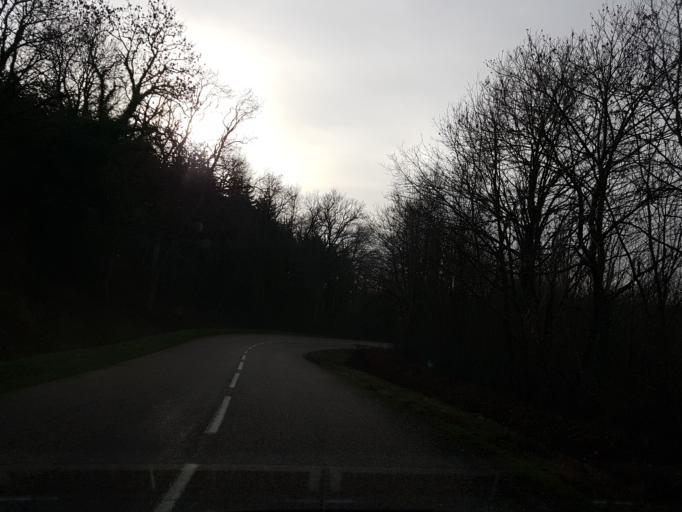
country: FR
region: Auvergne
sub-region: Departement de l'Allier
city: Souvigny
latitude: 46.4412
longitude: 3.0986
